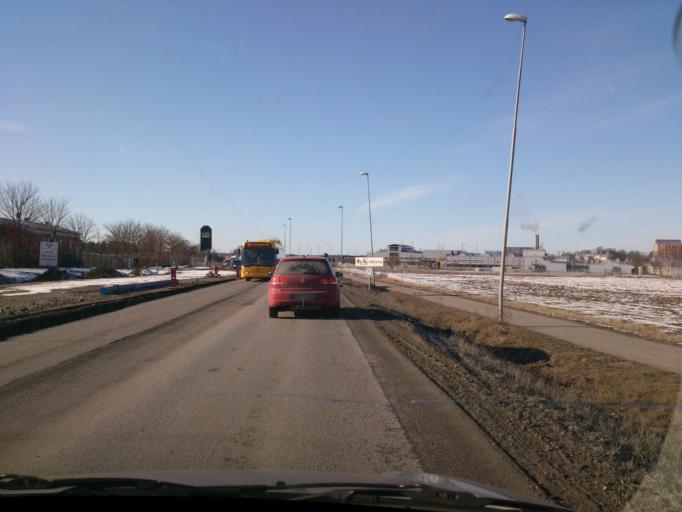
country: SE
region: Uppsala
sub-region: Uppsala Kommun
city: Saevja
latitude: 59.8464
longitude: 17.7159
